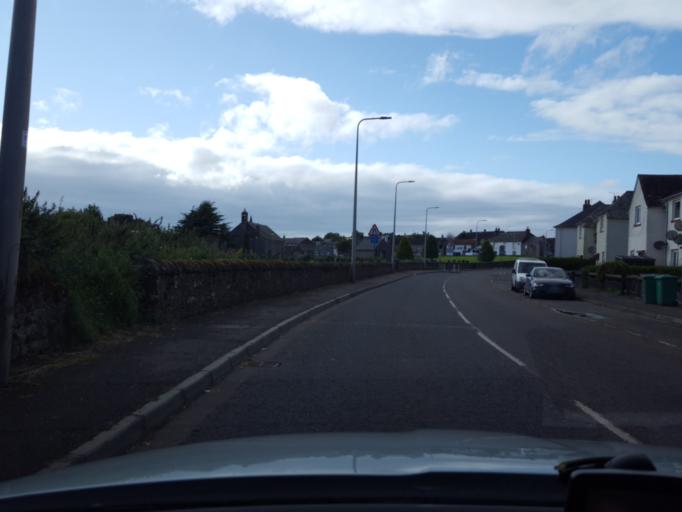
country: GB
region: Scotland
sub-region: Fife
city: Auchtermuchty
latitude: 56.2781
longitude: -3.2637
